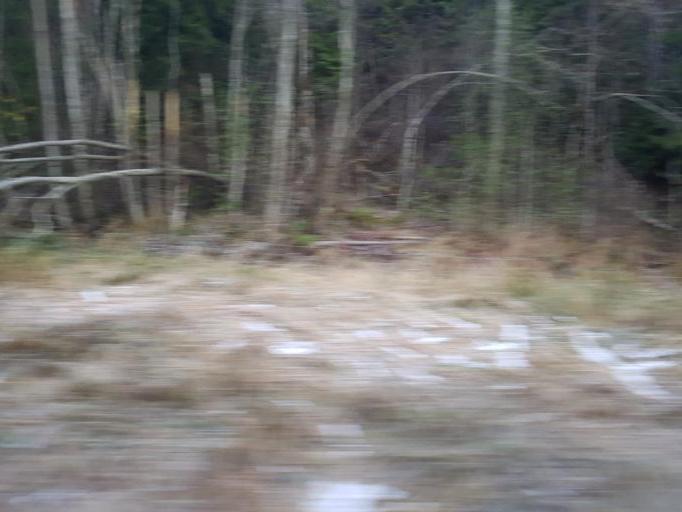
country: NO
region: Sor-Trondelag
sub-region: Midtre Gauldal
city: Storen
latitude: 63.0310
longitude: 10.2698
